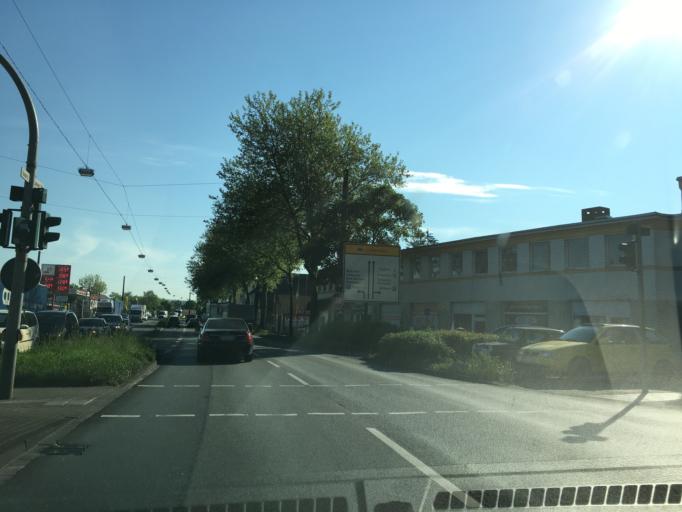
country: DE
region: North Rhine-Westphalia
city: Bad Oeynhausen
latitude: 52.2064
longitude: 8.8006
